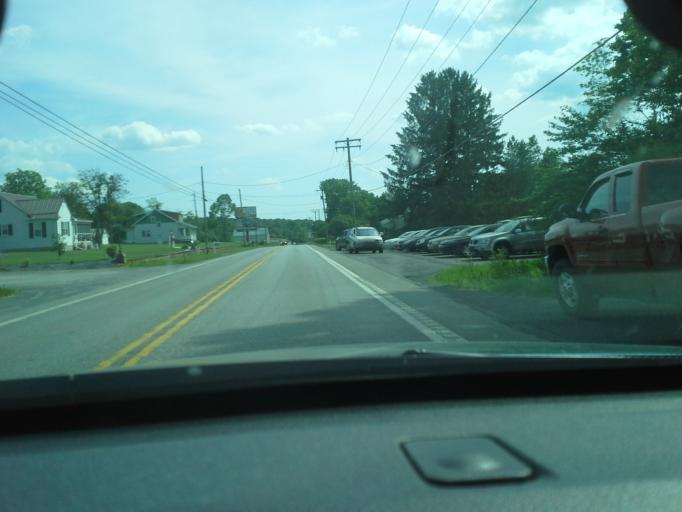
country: US
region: Pennsylvania
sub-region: Fulton County
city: McConnellsburg
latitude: 39.9651
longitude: -77.9767
